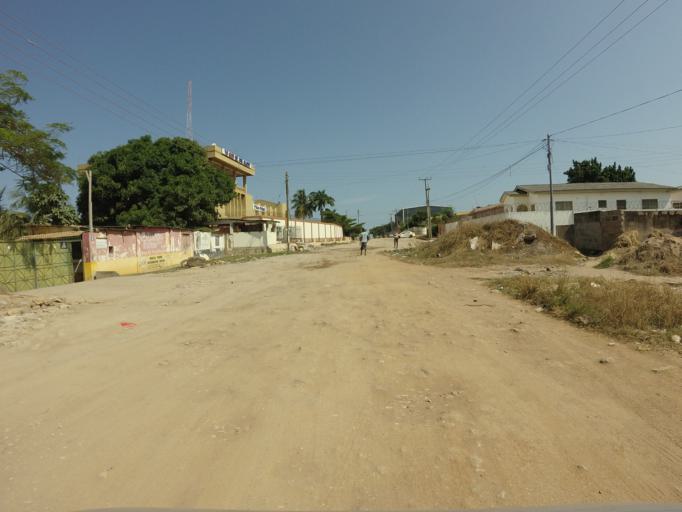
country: GH
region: Greater Accra
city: Dome
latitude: 5.6386
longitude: -0.2343
